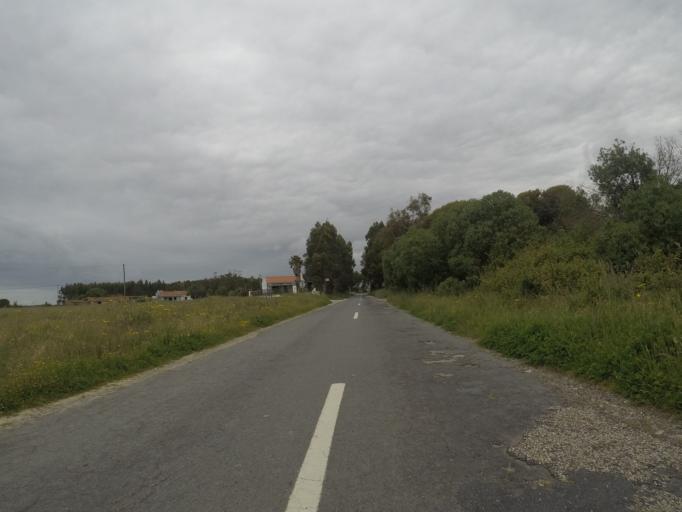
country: PT
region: Beja
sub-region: Odemira
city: Sao Teotonio
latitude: 37.5915
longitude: -8.7776
